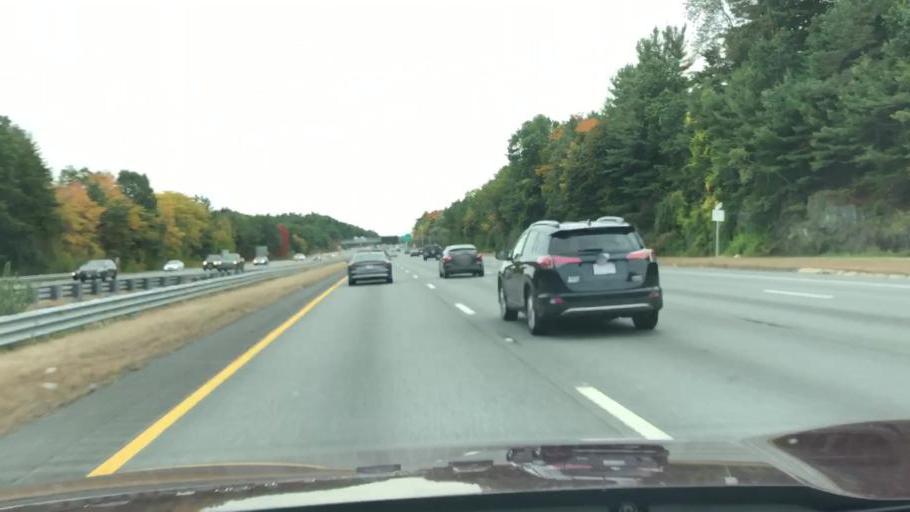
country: US
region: Massachusetts
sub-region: Middlesex County
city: Wilmington
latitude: 42.5745
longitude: -71.1504
